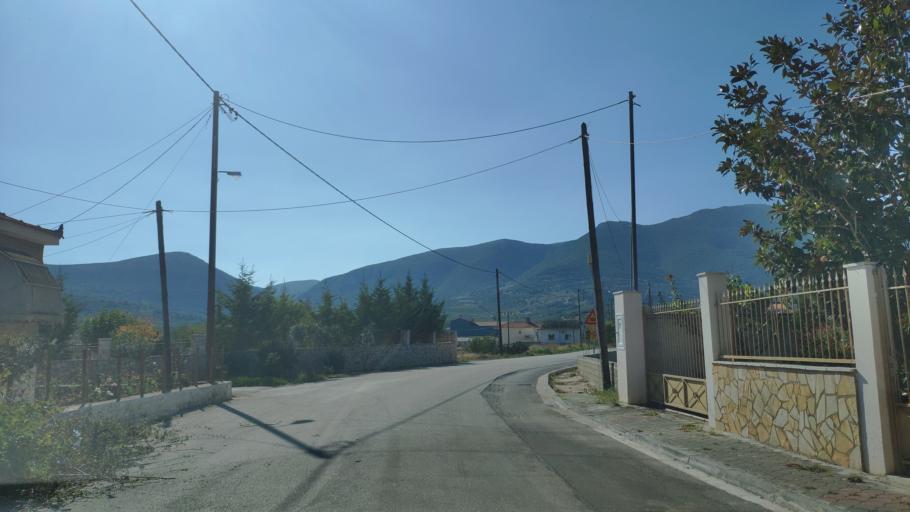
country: GR
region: Peloponnese
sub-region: Nomos Korinthias
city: Khiliomodhi
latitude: 37.8057
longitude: 22.8702
